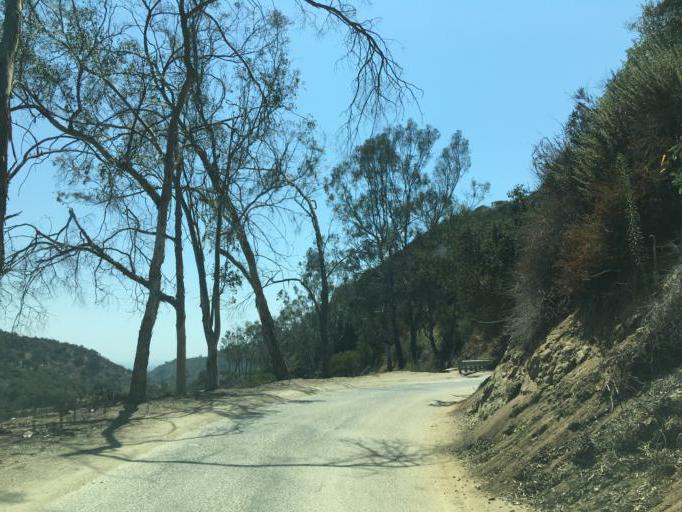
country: US
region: California
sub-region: Los Angeles County
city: Beverly Hills
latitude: 34.1133
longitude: -118.4159
